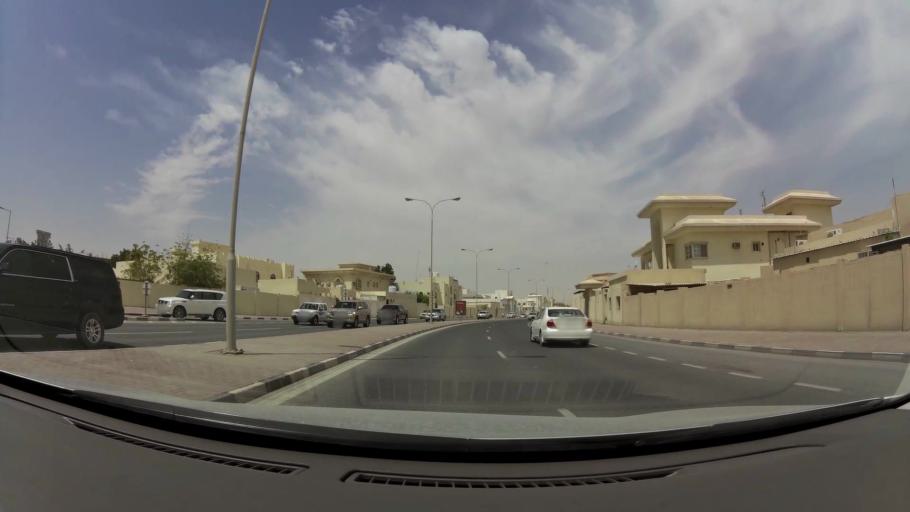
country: QA
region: Baladiyat ar Rayyan
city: Ar Rayyan
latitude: 25.2867
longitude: 51.4186
